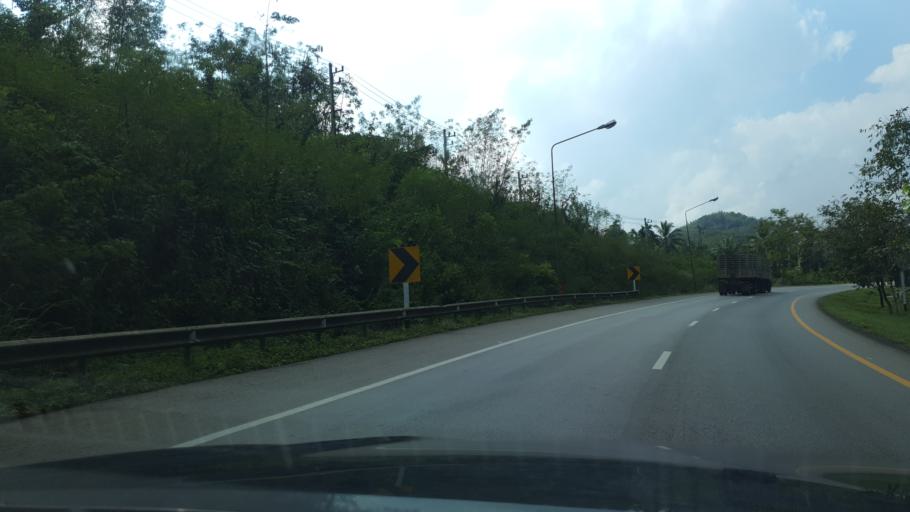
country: TH
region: Chumphon
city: Pathio
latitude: 10.8595
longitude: 99.2471
